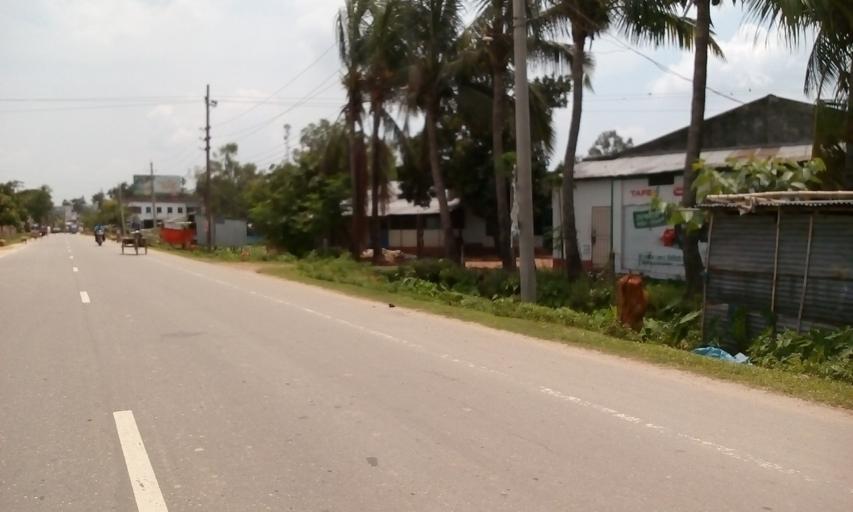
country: BD
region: Rangpur Division
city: Parbatipur
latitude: 25.5018
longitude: 88.9712
